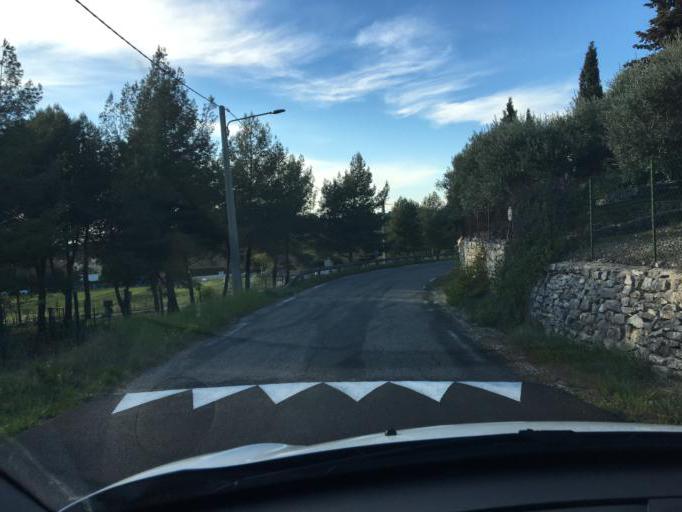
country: FR
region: Provence-Alpes-Cote d'Azur
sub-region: Departement du Vaucluse
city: Villes-sur-Auzon
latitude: 44.0546
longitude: 5.2377
